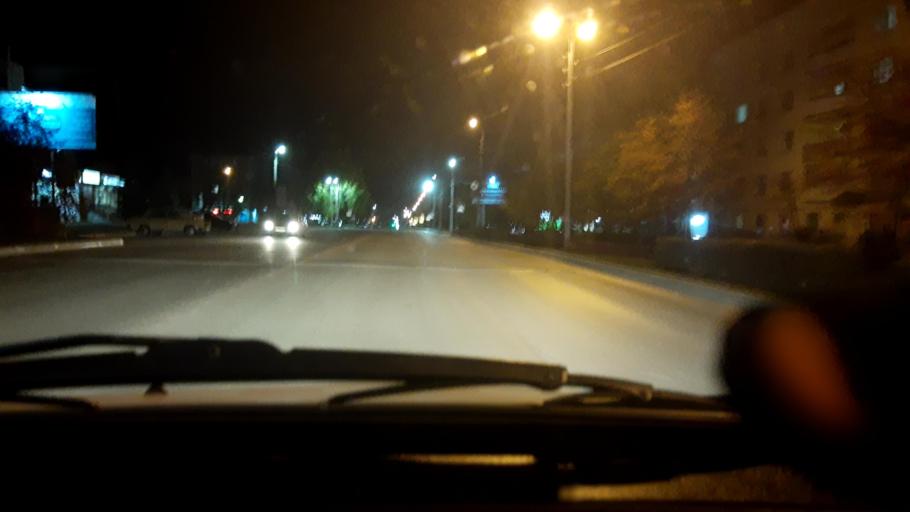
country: RU
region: Bashkortostan
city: Belebey
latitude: 54.0989
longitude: 54.1049
